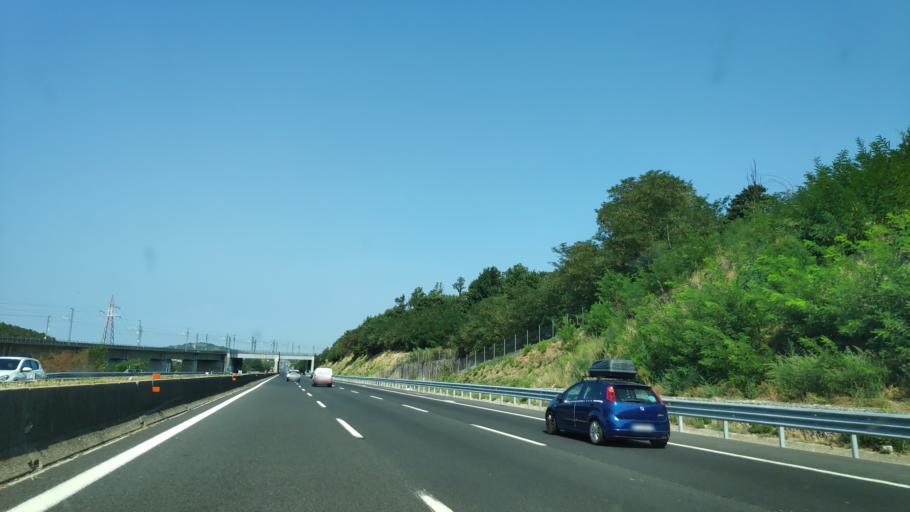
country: IT
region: Campania
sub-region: Provincia di Caserta
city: Bivio Mortola
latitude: 41.4220
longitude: 13.9258
